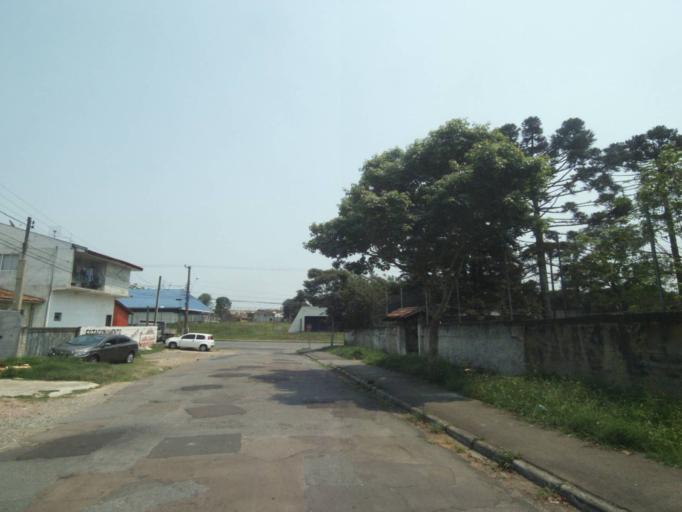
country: BR
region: Parana
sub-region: Sao Jose Dos Pinhais
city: Sao Jose dos Pinhais
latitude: -25.5301
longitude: -49.2407
